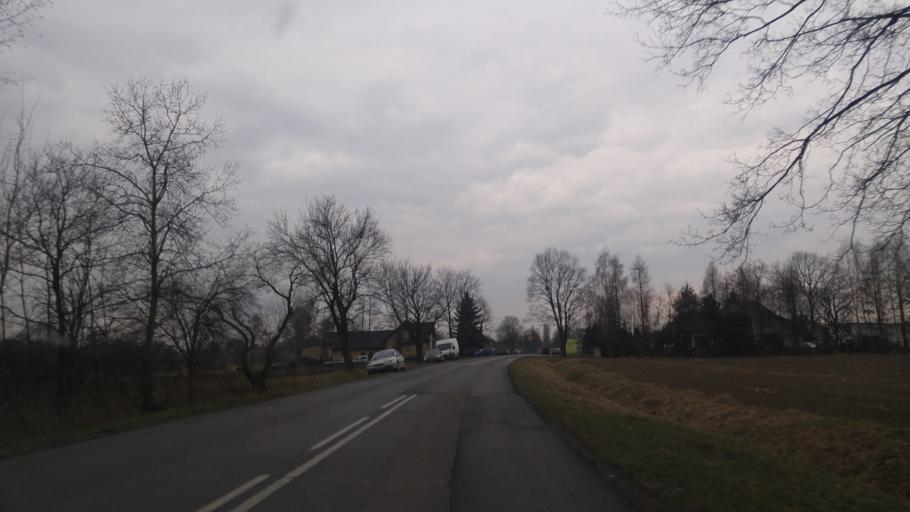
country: PL
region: Silesian Voivodeship
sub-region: Powiat cieszynski
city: Strumien
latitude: 49.9254
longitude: 18.7835
